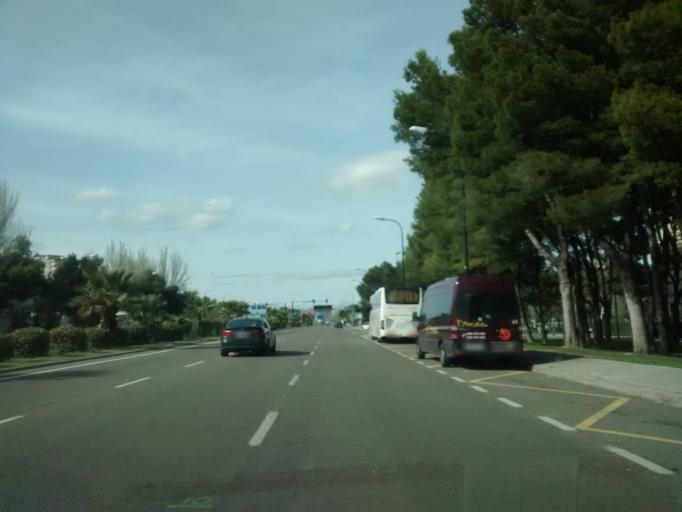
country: ES
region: Aragon
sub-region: Provincia de Zaragoza
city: Zaragoza
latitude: 41.6624
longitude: -0.8808
